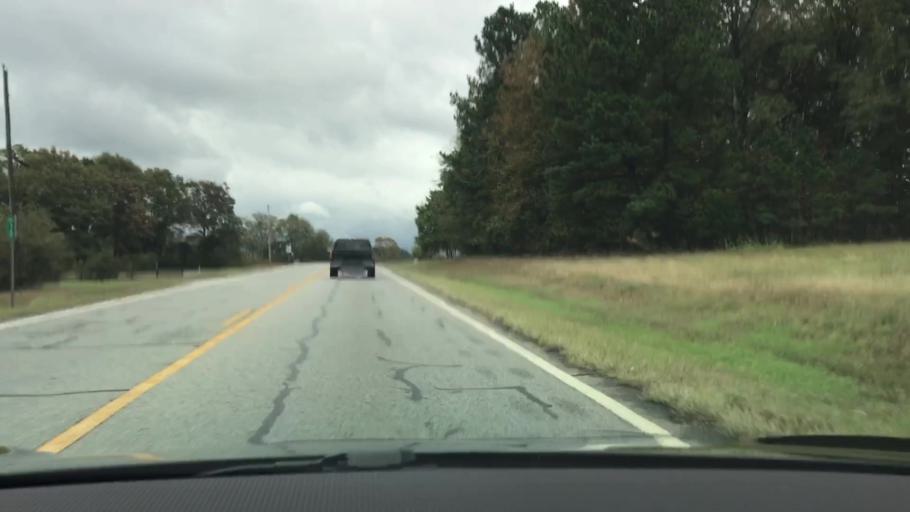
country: US
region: Georgia
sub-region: Oconee County
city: Watkinsville
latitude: 33.8455
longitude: -83.3904
